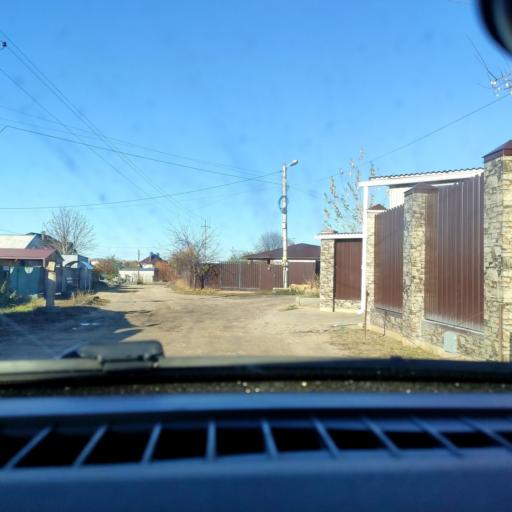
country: RU
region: Voronezj
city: Podgornoye
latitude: 51.7248
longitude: 39.1469
